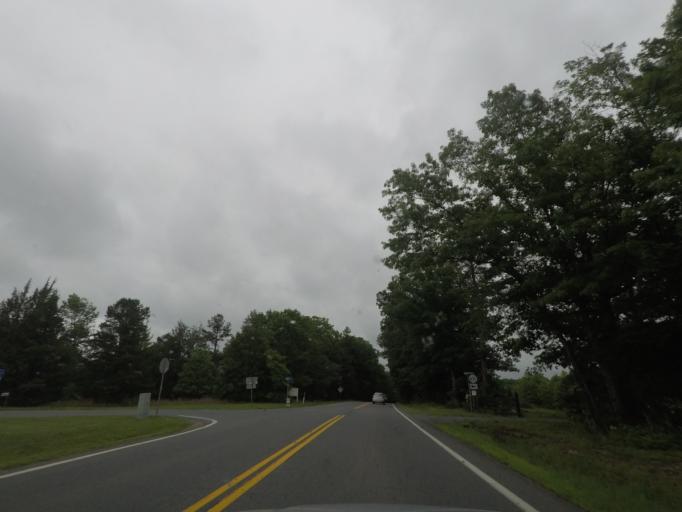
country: US
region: Virginia
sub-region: Fluvanna County
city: Palmyra
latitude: 37.9422
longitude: -78.2444
